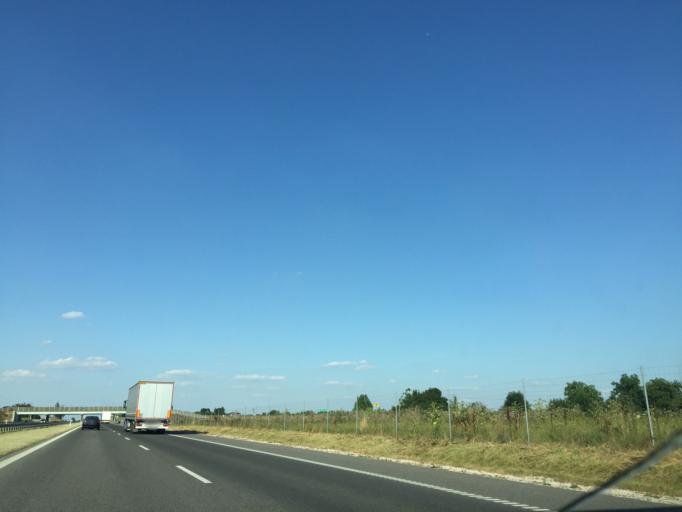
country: PL
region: Swietokrzyskie
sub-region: Powiat jedrzejowski
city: Jedrzejow
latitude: 50.5880
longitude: 20.2419
